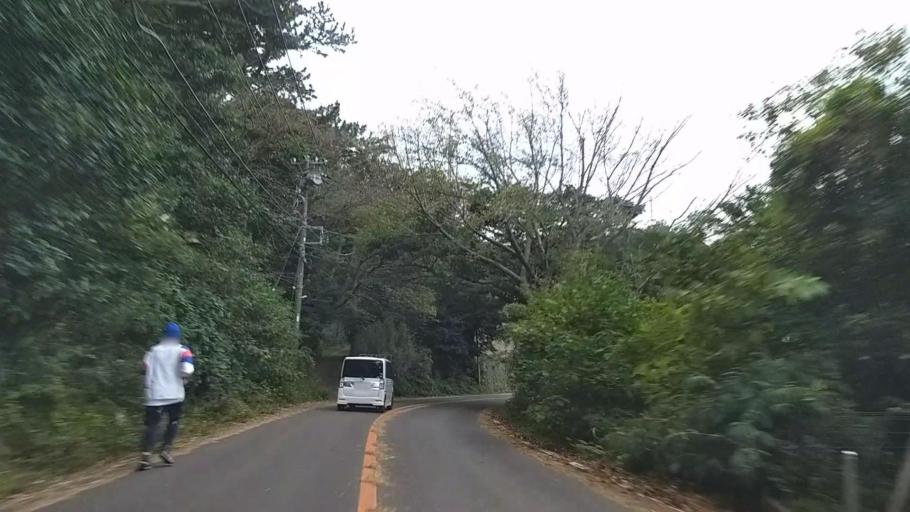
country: JP
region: Kanagawa
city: Yugawara
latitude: 35.1463
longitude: 139.1482
